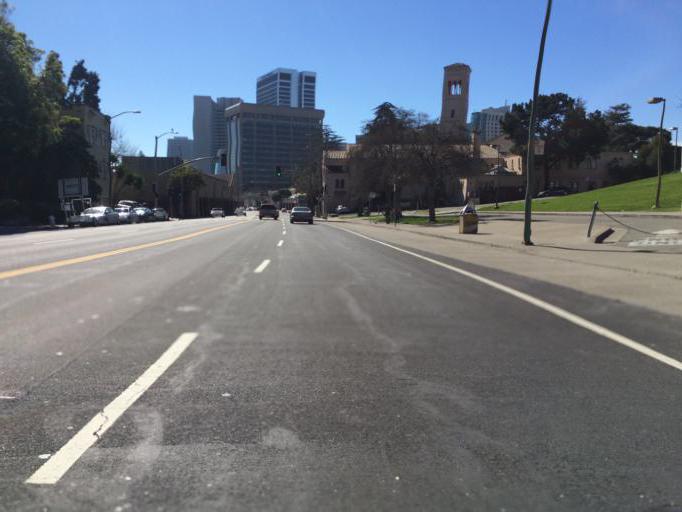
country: US
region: California
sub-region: Alameda County
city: Oakland
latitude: 37.8144
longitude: -122.2600
